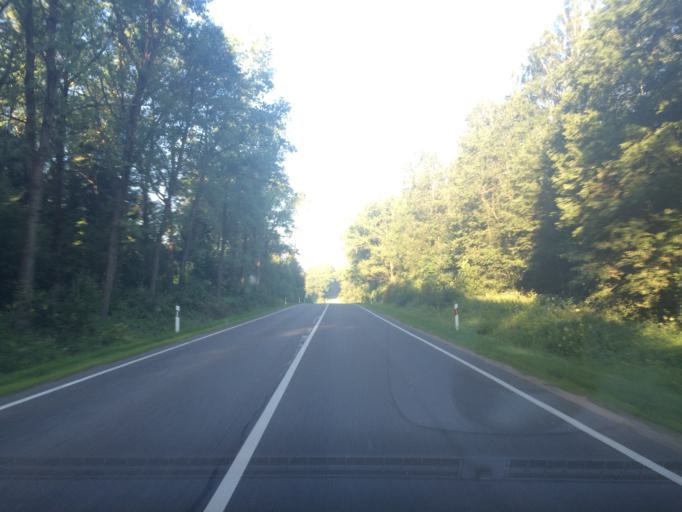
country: LT
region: Utenos apskritis
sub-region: Anyksciai
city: Anyksciai
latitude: 55.3996
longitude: 25.0914
